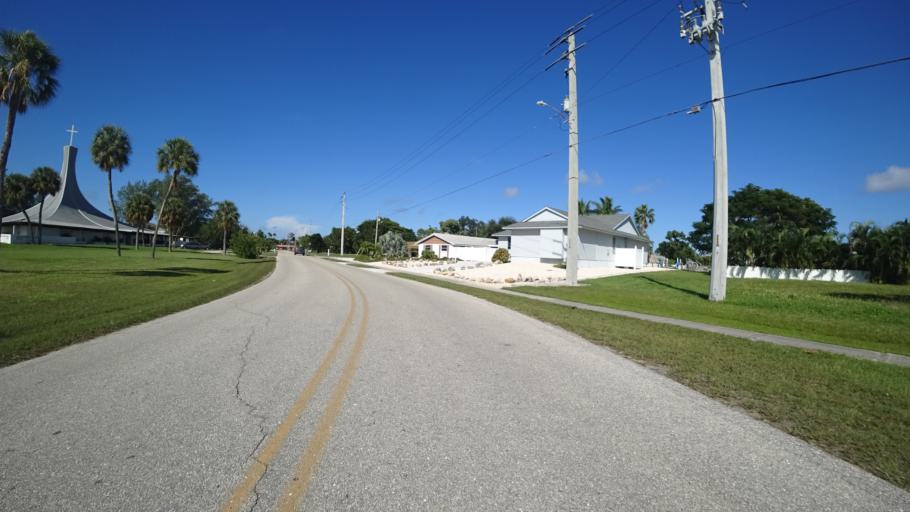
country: US
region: Florida
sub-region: Manatee County
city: Holmes Beach
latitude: 27.5146
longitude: -82.7187
